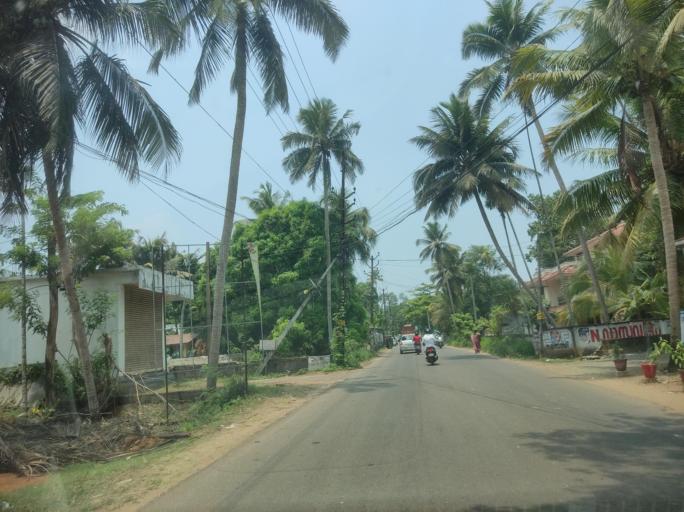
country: IN
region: Kerala
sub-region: Kottayam
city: Kottayam
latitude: 9.5949
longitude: 76.4753
